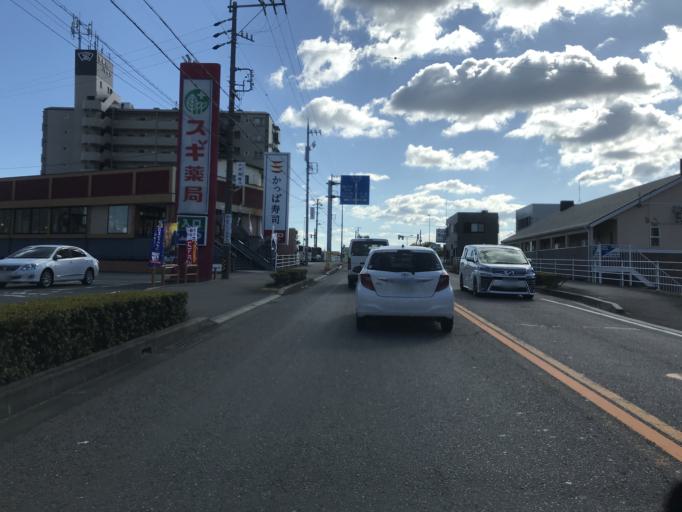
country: JP
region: Aichi
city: Nagoya-shi
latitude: 35.2067
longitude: 136.8569
